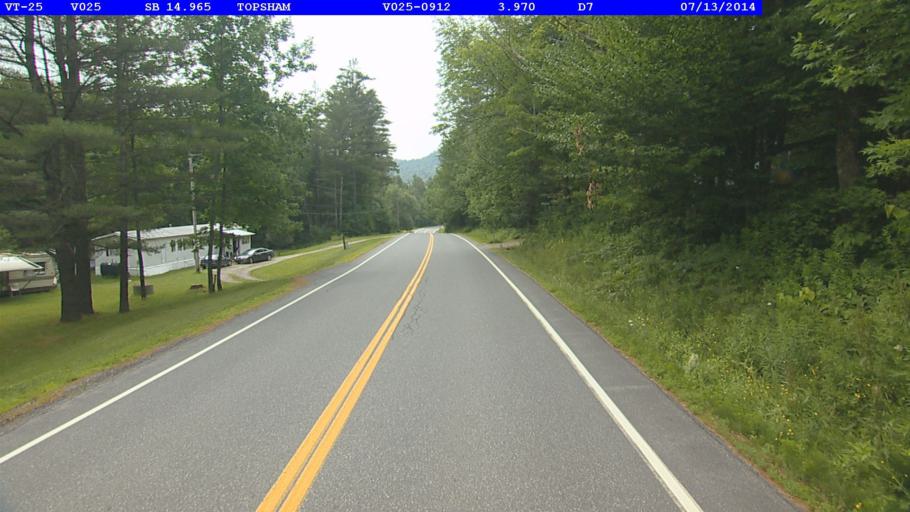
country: US
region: Vermont
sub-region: Orange County
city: Chelsea
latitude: 44.1076
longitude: -72.3188
